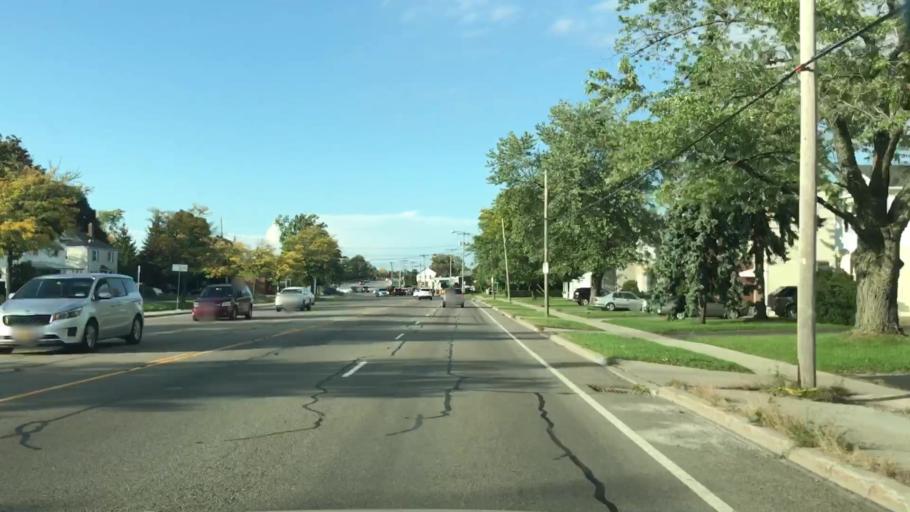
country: US
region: New York
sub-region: Erie County
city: Williamsville
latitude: 42.9474
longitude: -78.7543
